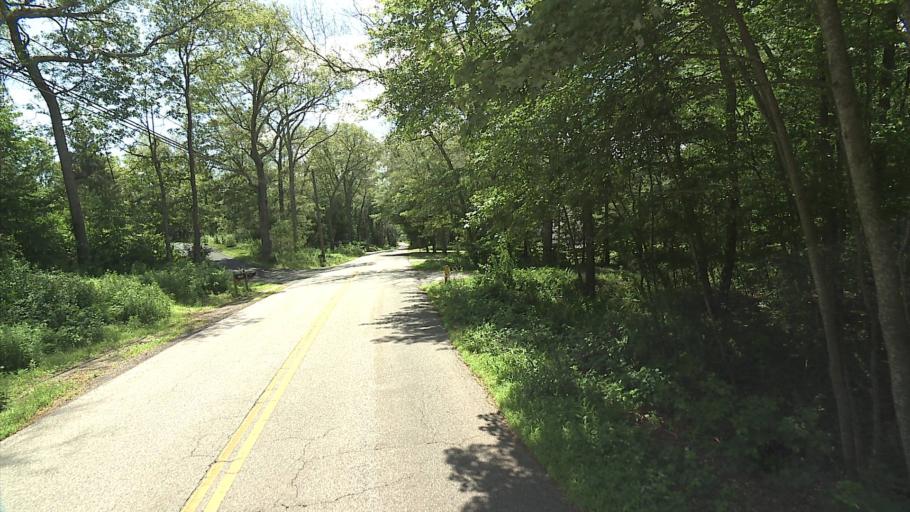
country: US
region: Connecticut
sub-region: New London County
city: Preston City
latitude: 41.5289
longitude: -71.8801
